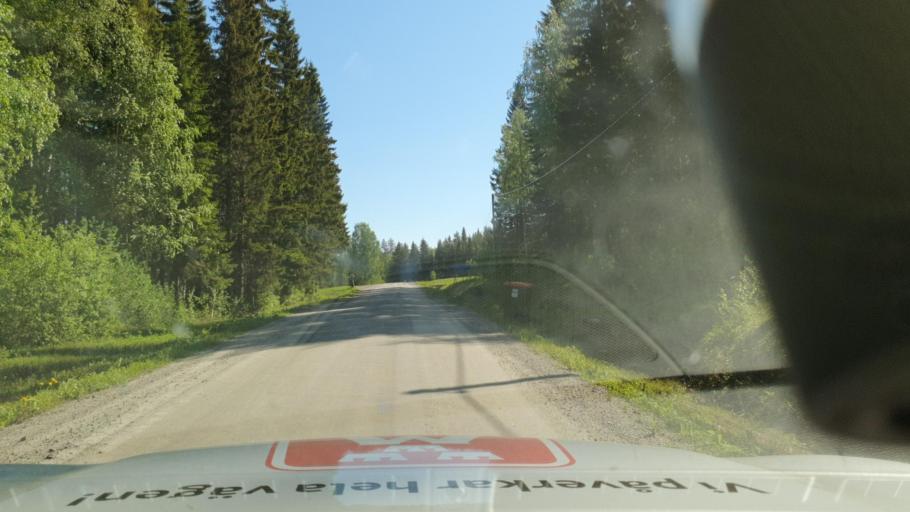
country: SE
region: Vaesterbotten
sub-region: Vannas Kommun
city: Vaennaes
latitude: 63.9872
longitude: 19.7446
